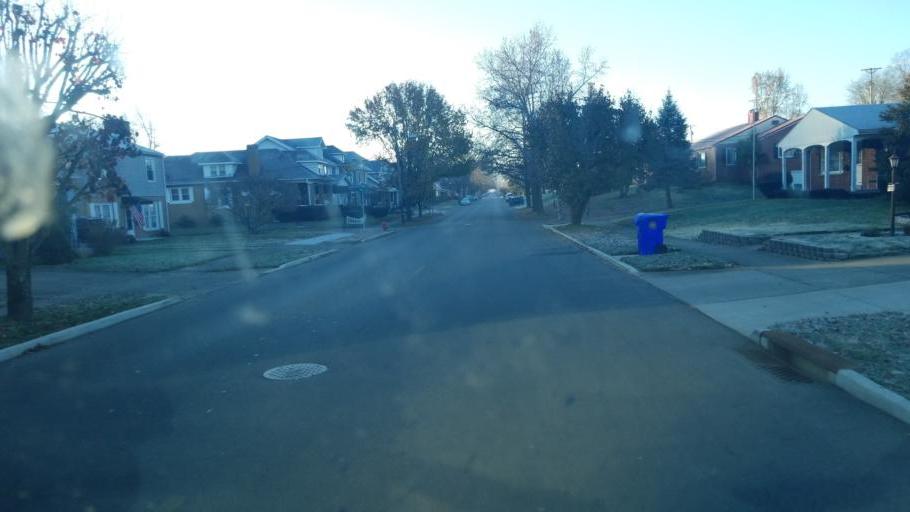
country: US
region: Ohio
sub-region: Scioto County
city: Portsmouth
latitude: 38.7503
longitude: -82.9749
